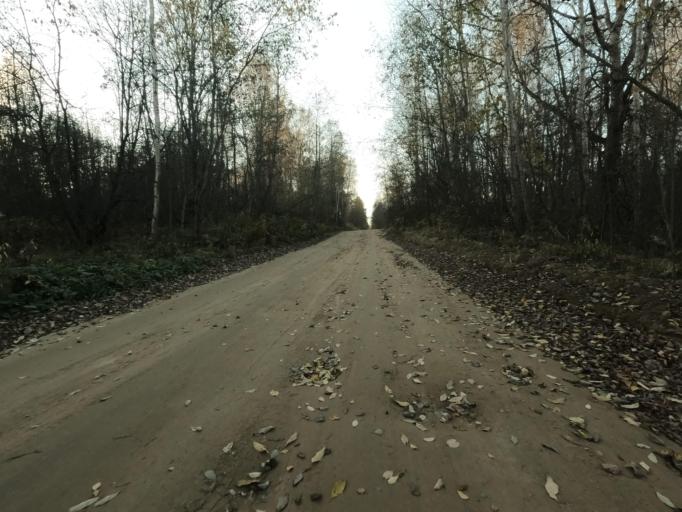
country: RU
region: Leningrad
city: Mga
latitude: 59.7597
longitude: 31.2642
